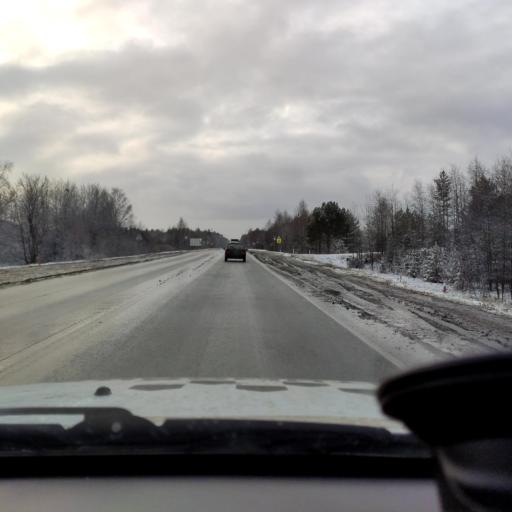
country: RU
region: Perm
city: Chaykovskaya
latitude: 58.0293
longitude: 55.5517
